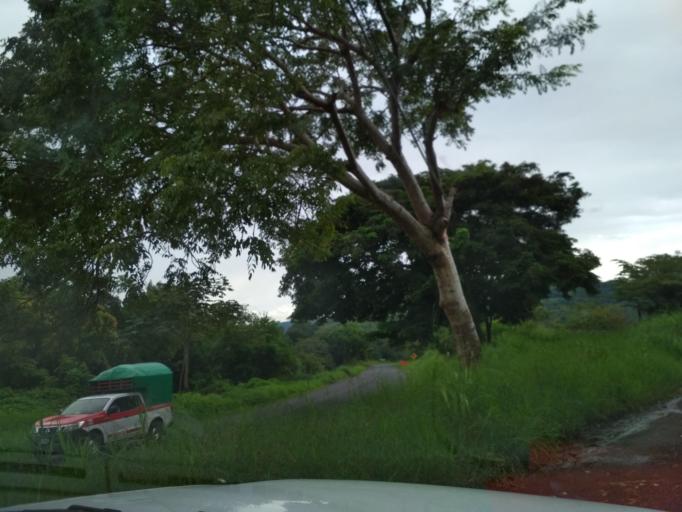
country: MX
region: Veracruz
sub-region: San Andres Tuxtla
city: Los Pinos
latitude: 18.4462
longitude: -95.2332
